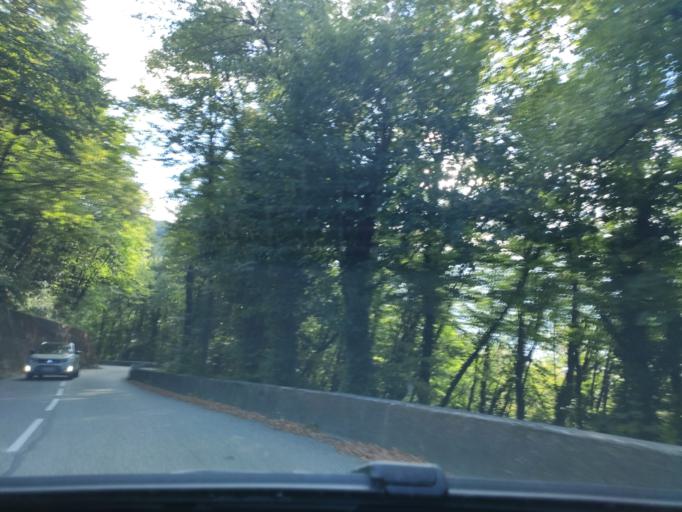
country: FR
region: Rhone-Alpes
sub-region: Departement de l'Isere
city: Gieres
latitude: 45.1792
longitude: 5.7931
